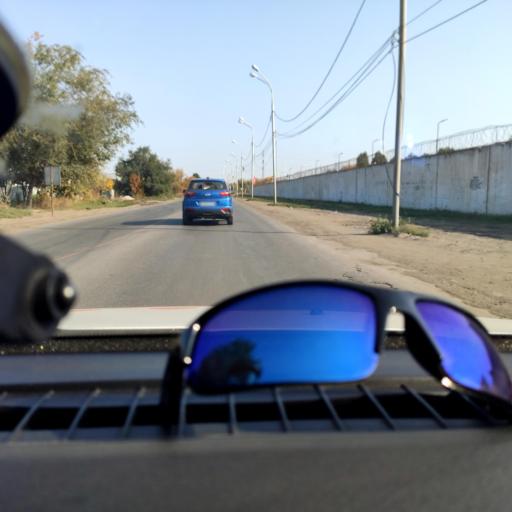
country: RU
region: Samara
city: Samara
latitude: 53.1355
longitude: 50.1085
